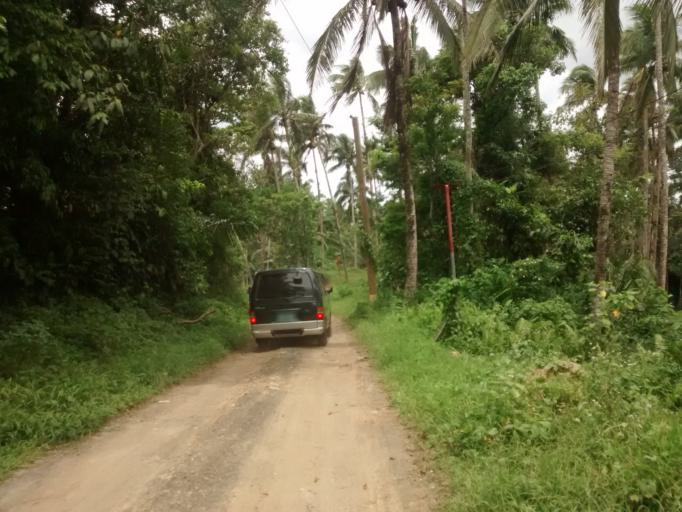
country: PH
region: Calabarzon
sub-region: Province of Laguna
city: Luisiana
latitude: 14.1594
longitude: 121.5480
